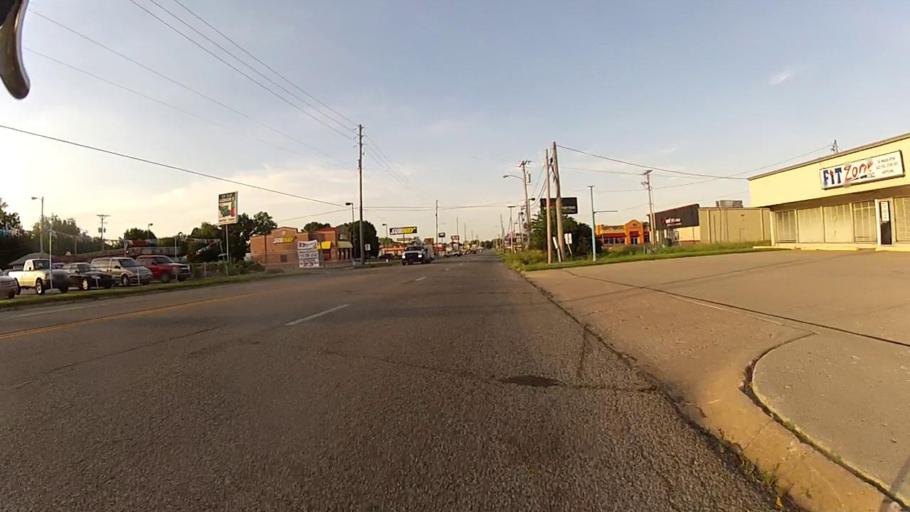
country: US
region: Kansas
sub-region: Cowley County
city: Arkansas City
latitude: 37.0841
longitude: -97.0402
